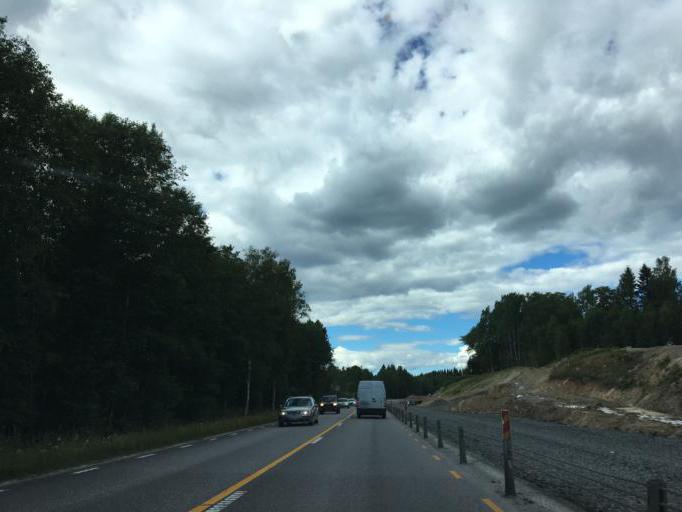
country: SE
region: OErebro
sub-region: Askersunds Kommun
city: Asbro
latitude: 58.9320
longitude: 14.9999
